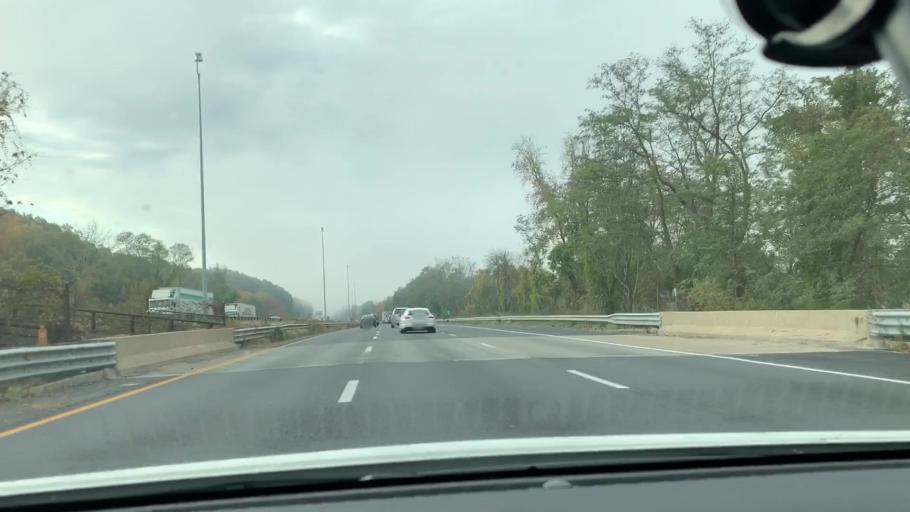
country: US
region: Massachusetts
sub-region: Hampden County
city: Longmeadow
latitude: 42.0578
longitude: -72.5894
